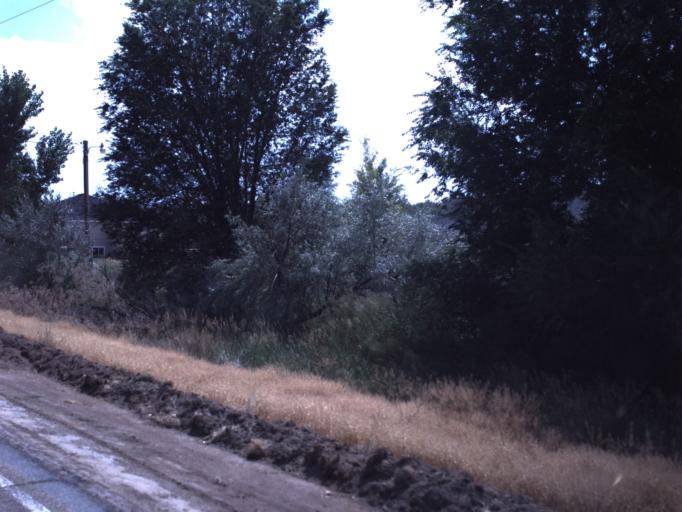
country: US
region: Utah
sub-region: Duchesne County
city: Roosevelt
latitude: 40.3307
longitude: -110.0202
